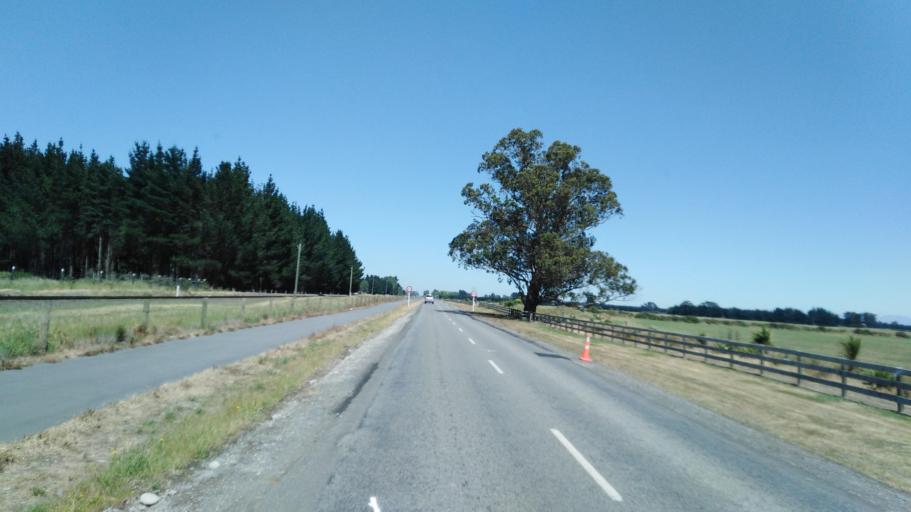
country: NZ
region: Canterbury
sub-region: Selwyn District
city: Prebbleton
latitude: -43.5609
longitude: 172.4562
